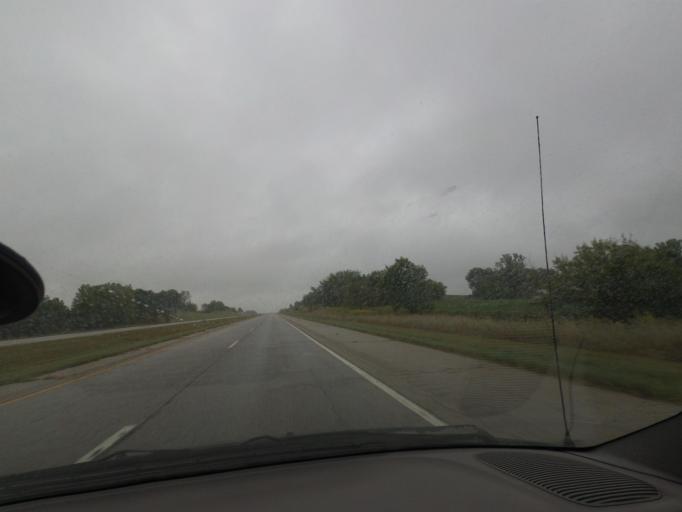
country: US
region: Illinois
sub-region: Pike County
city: Barry
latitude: 39.7080
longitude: -91.0525
